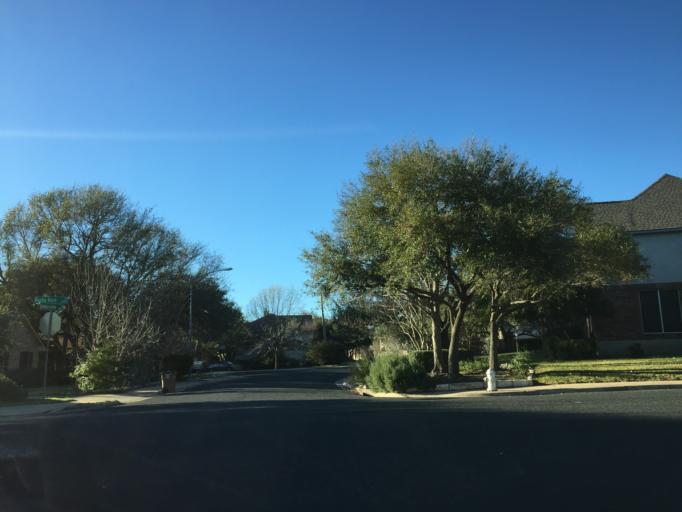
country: US
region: Texas
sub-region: Williamson County
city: Jollyville
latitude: 30.4336
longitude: -97.7849
